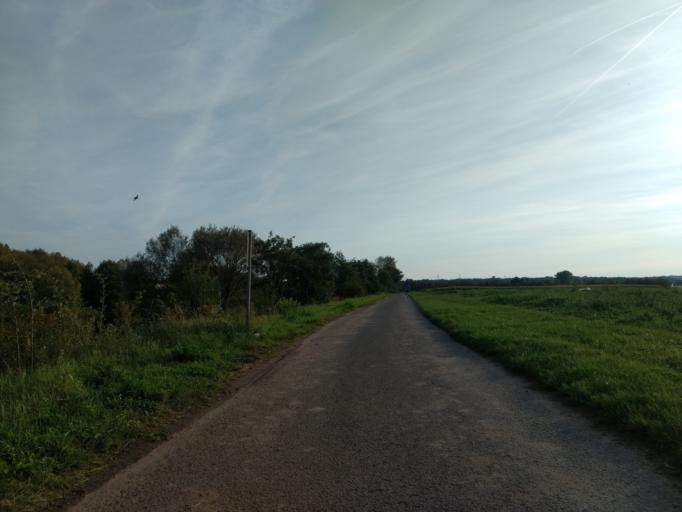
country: DE
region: Saarland
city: Ensdorf
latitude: 49.3143
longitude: 6.7717
